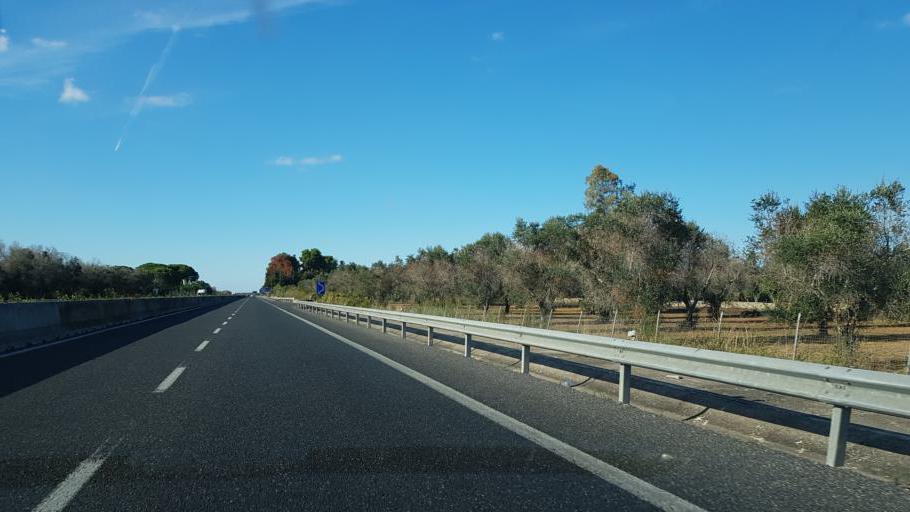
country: IT
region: Apulia
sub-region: Provincia di Brindisi
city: Torchiarolo
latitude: 40.4748
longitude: 18.0484
